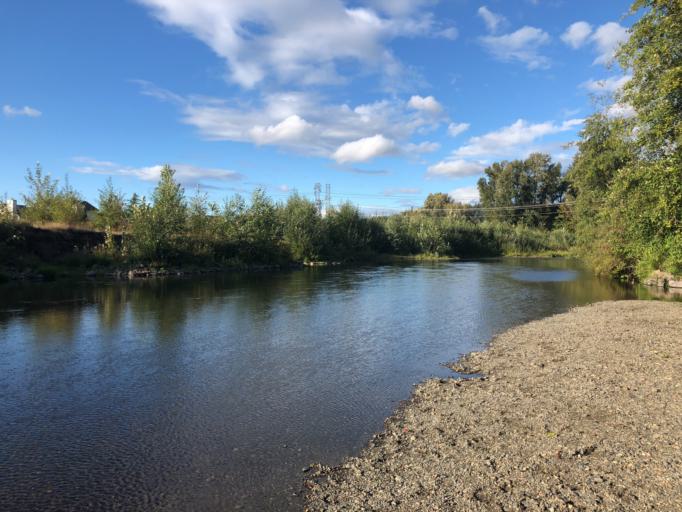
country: US
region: Washington
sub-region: King County
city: Auburn
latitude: 47.3338
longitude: -122.2122
